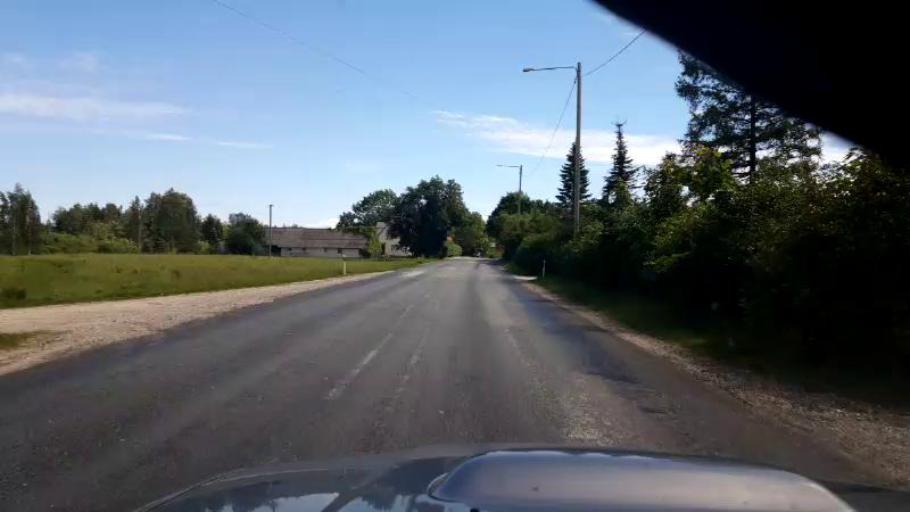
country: EE
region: Laeaene-Virumaa
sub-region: Rakke vald
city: Rakke
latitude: 58.9113
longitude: 26.2742
